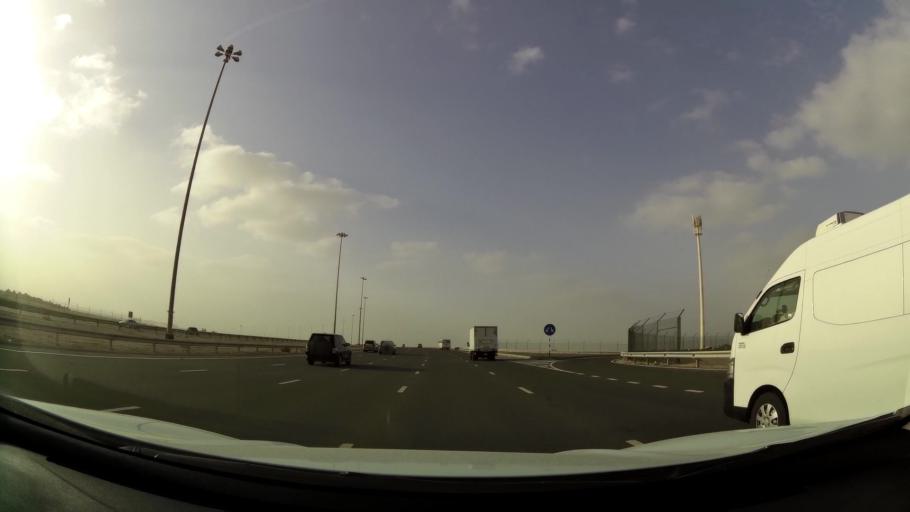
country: AE
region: Abu Dhabi
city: Abu Dhabi
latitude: 24.5408
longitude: 54.4835
